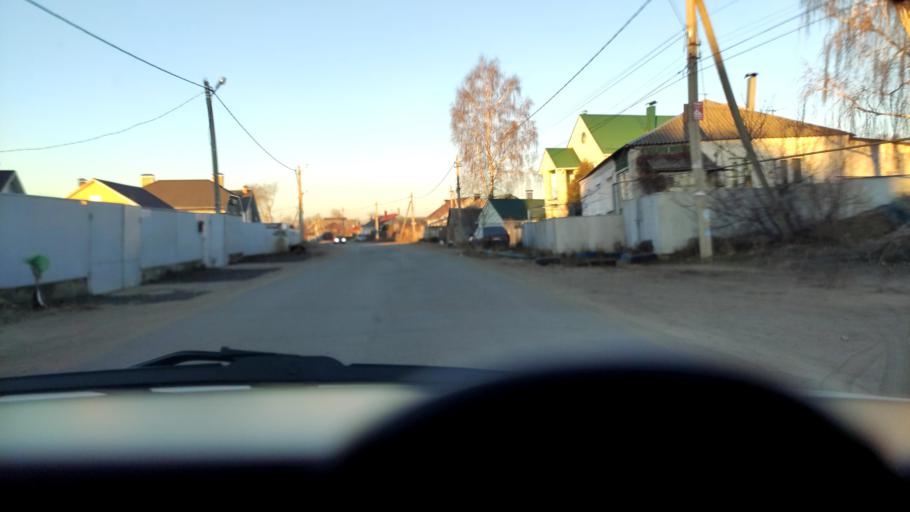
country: RU
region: Voronezj
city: Podgornoye
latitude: 51.7392
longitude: 39.1538
